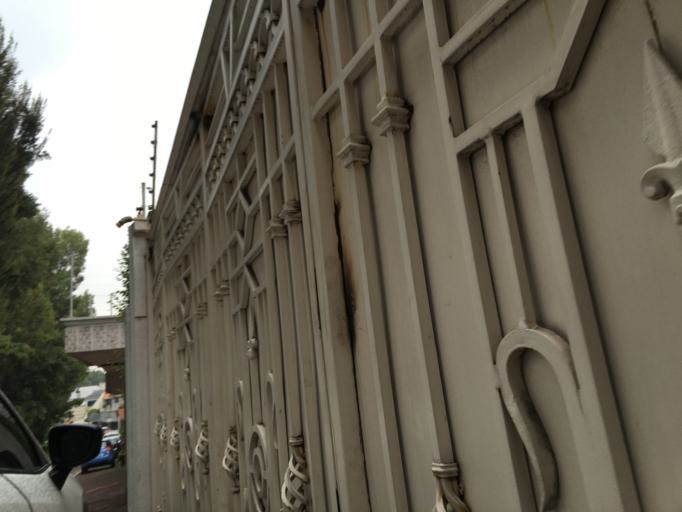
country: MX
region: Mexico City
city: Tlalpan
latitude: 19.2799
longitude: -99.1493
